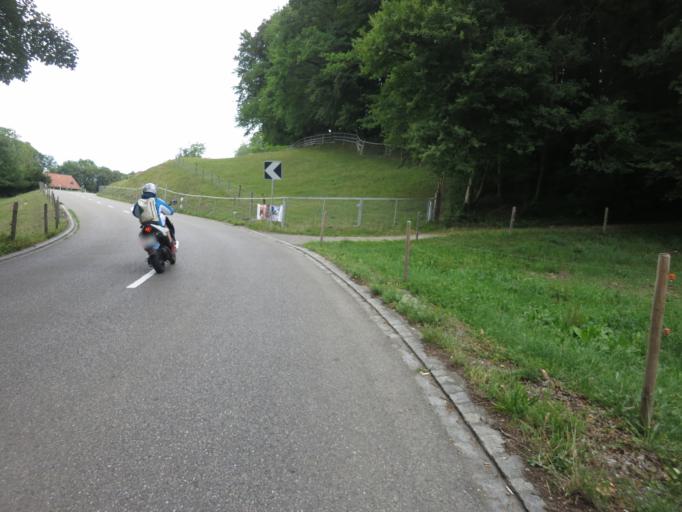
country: CH
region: Saint Gallen
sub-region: Wahlkreis Wil
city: Jonschwil
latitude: 47.4168
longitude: 9.0856
